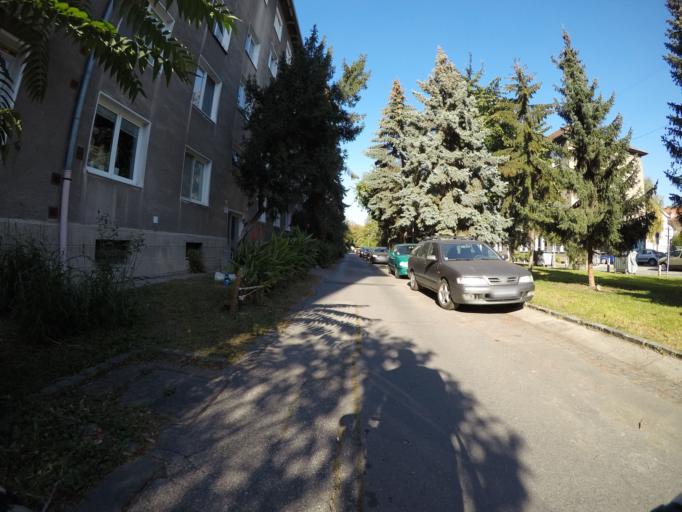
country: SK
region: Bratislavsky
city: Bratislava
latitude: 48.1484
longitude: 17.1264
